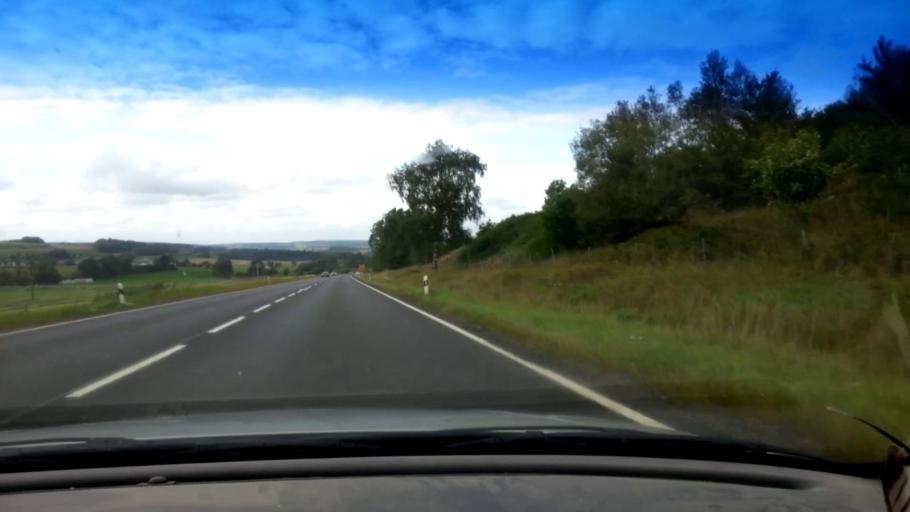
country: DE
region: Bavaria
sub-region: Upper Palatinate
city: Pechbrunn
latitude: 49.9804
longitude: 12.1324
